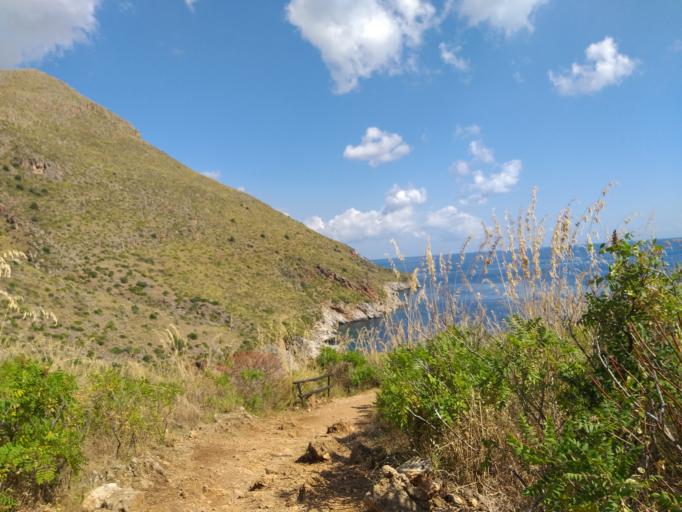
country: IT
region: Sicily
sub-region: Trapani
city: Castelluzzo
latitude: 38.0860
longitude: 12.8062
